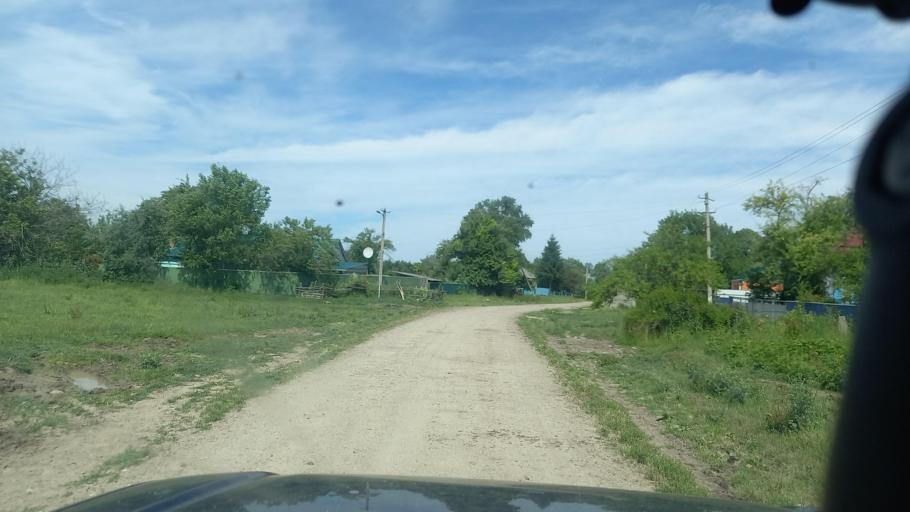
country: RU
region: Karachayevo-Cherkesiya
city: Kurdzhinovo
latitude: 44.1428
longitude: 41.0536
